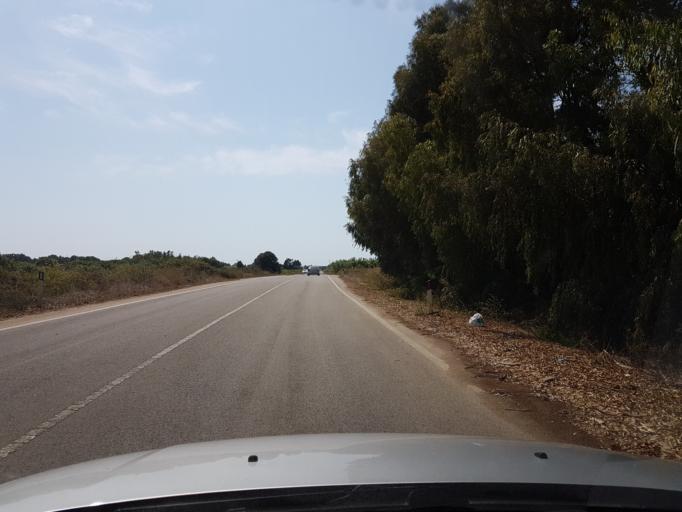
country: IT
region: Sardinia
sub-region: Provincia di Oristano
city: Cabras
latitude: 39.9199
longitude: 8.5435
